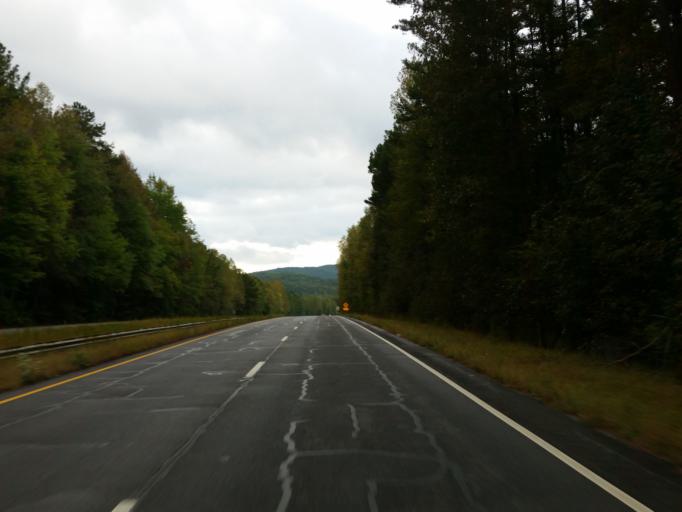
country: US
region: Georgia
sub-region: Bartow County
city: Emerson
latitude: 34.1020
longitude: -84.7445
